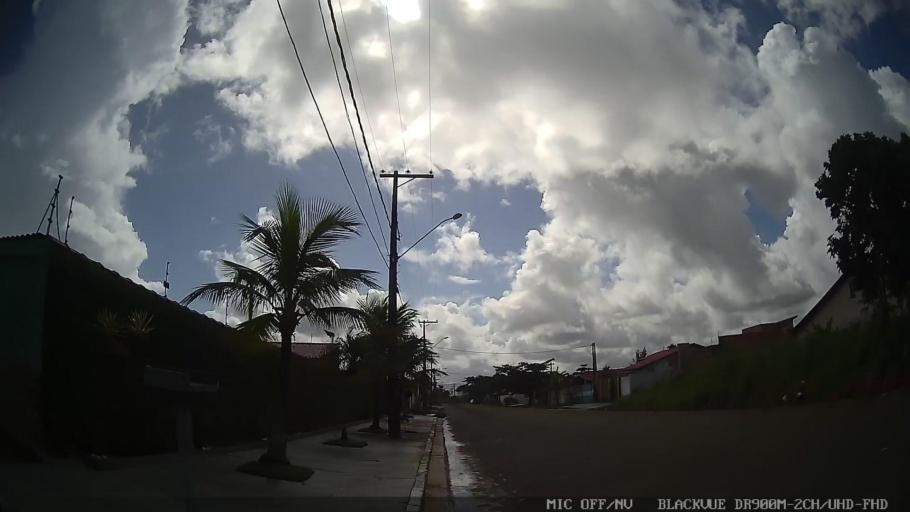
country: BR
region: Sao Paulo
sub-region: Itanhaem
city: Itanhaem
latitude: -24.2094
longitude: -46.8367
